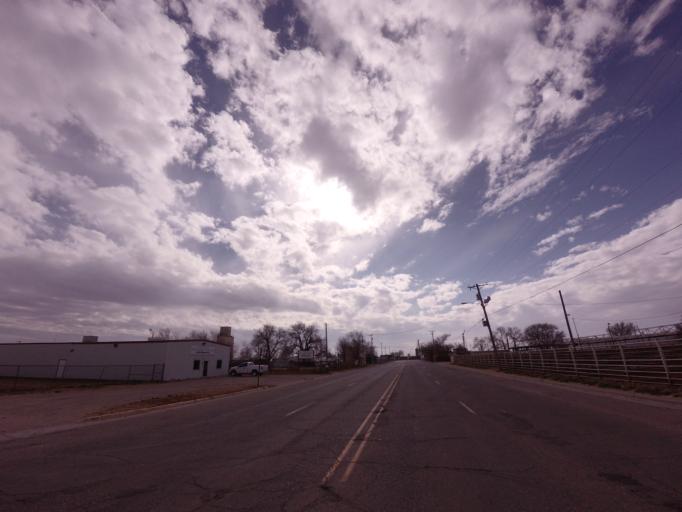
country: US
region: New Mexico
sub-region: Curry County
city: Clovis
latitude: 34.3928
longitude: -103.2205
